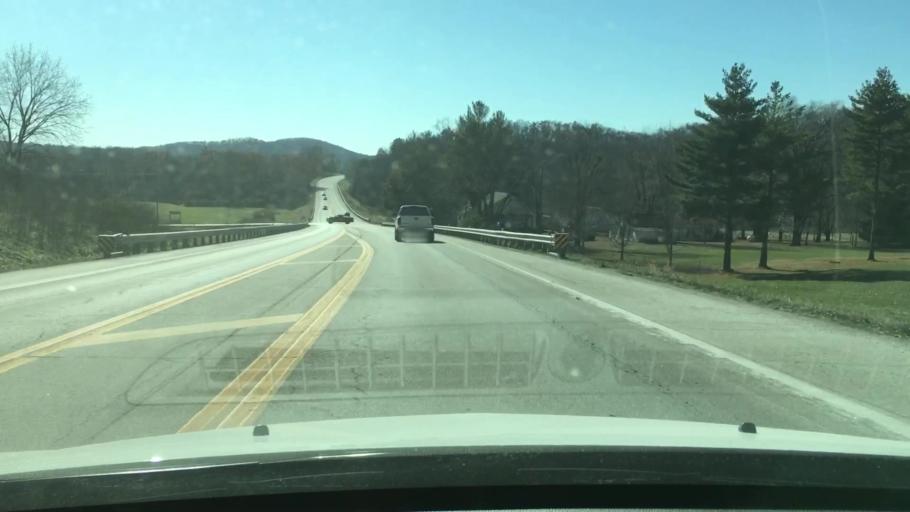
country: US
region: Missouri
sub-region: Pike County
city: Louisiana
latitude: 39.4394
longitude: -91.0792
